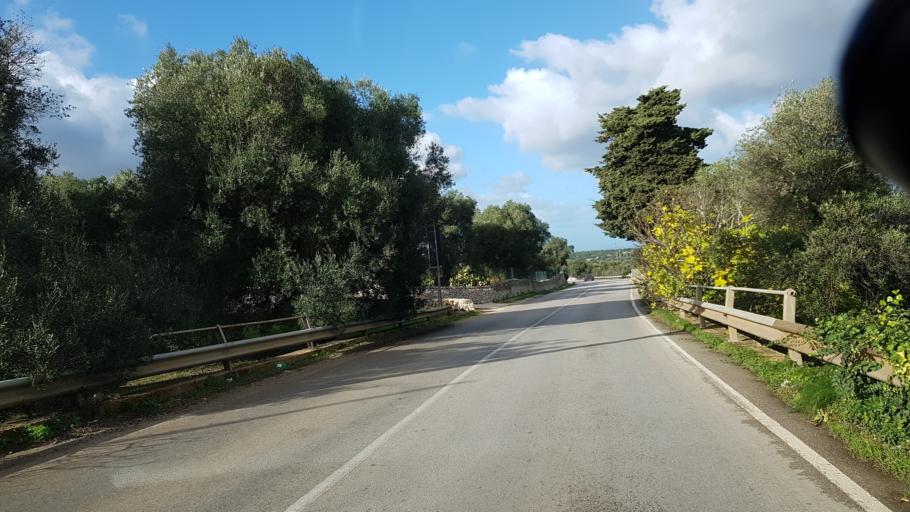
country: IT
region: Apulia
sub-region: Provincia di Brindisi
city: Ostuni
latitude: 40.7338
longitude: 17.5672
